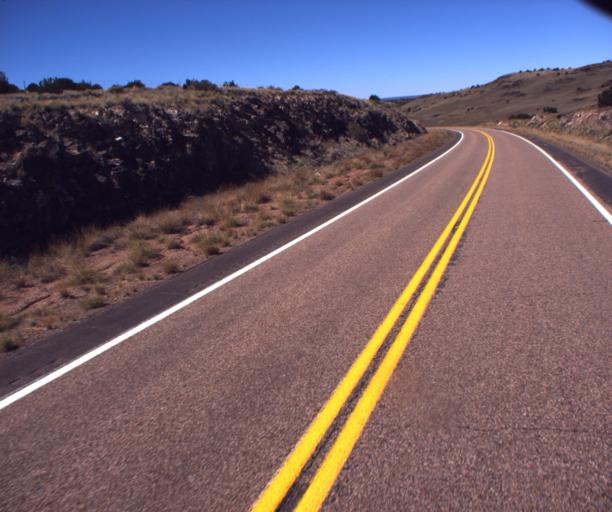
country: US
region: Arizona
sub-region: Apache County
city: Saint Johns
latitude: 34.5681
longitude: -109.5115
